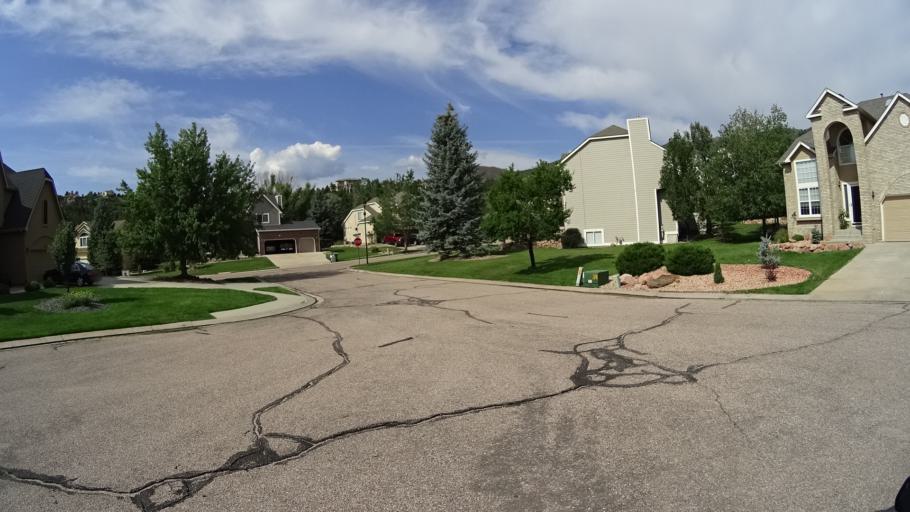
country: US
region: Colorado
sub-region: El Paso County
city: Air Force Academy
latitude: 38.9442
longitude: -104.8662
